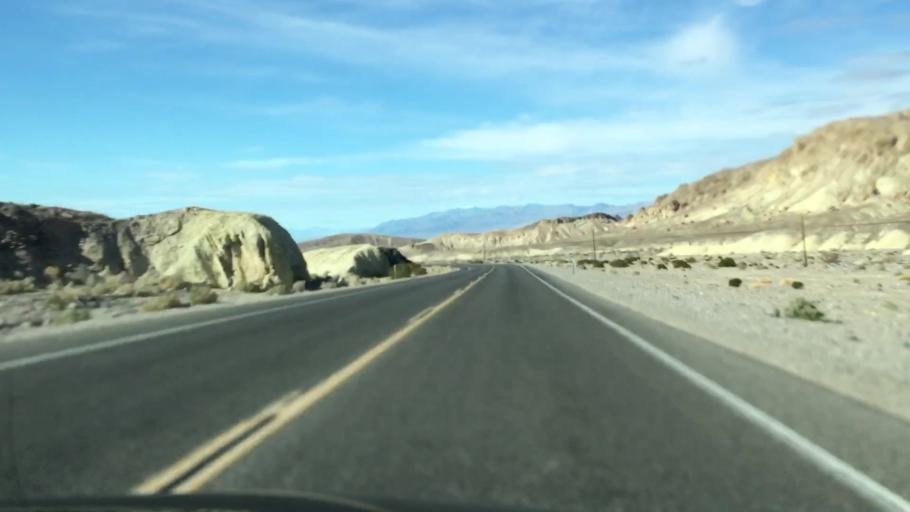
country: US
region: Nevada
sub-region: Nye County
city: Beatty
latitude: 36.3889
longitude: -116.7578
